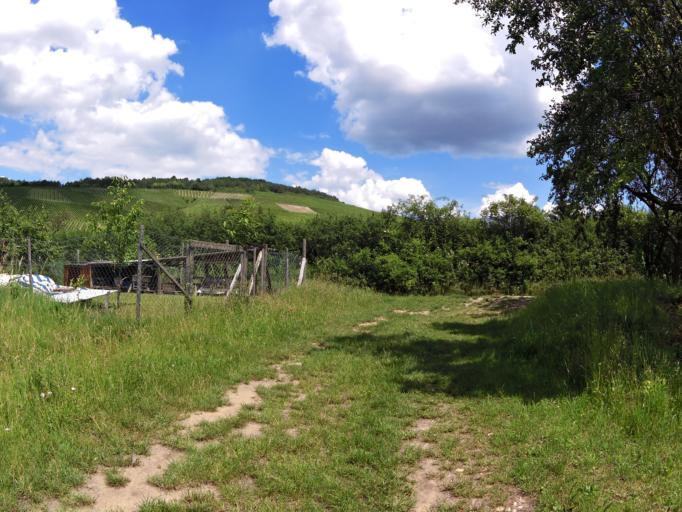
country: DE
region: Bavaria
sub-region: Regierungsbezirk Unterfranken
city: Thungersheim
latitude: 49.8871
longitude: 9.8405
